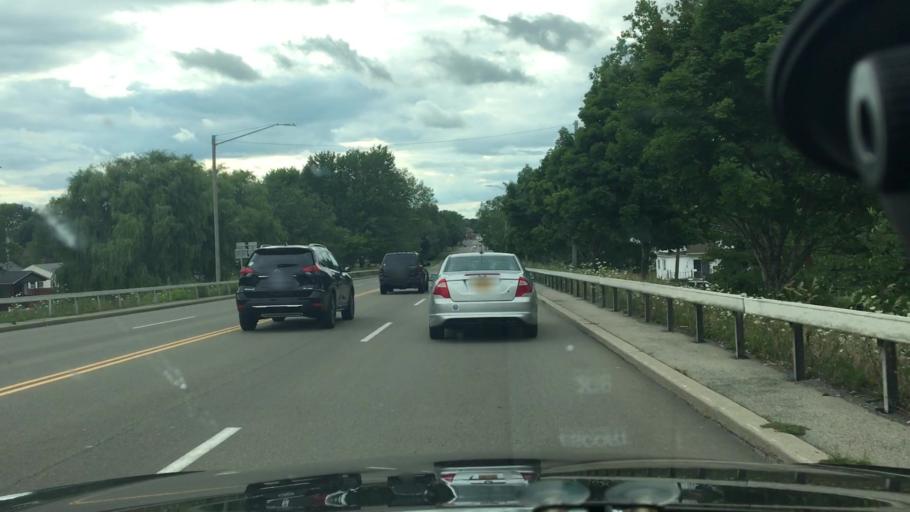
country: US
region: New York
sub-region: Erie County
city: West Seneca
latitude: 42.8282
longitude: -78.7949
